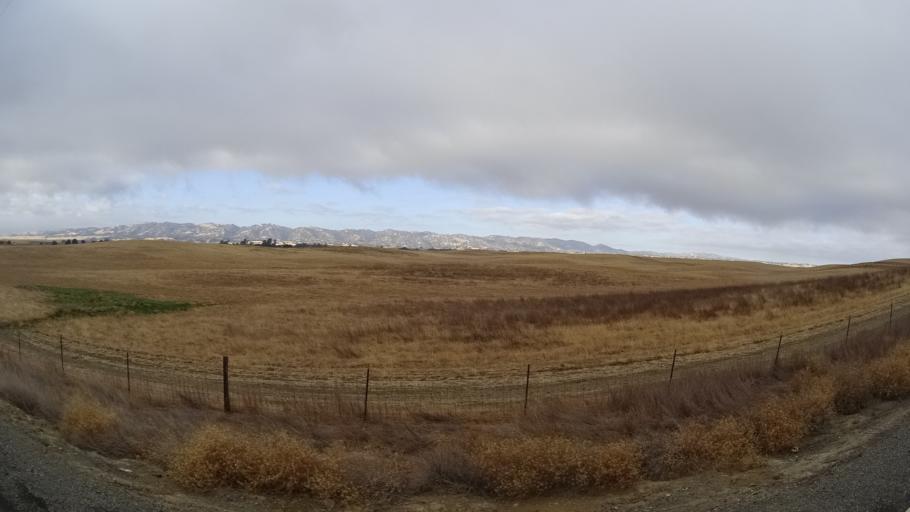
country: US
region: California
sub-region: Yolo County
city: Dunnigan
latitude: 38.8223
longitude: -122.0432
